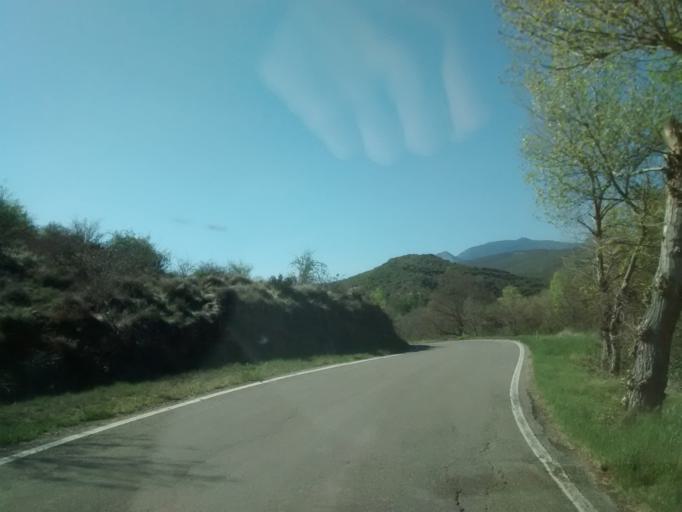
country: ES
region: Aragon
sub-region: Provincia de Huesca
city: Ibieca
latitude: 42.2134
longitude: -0.1959
